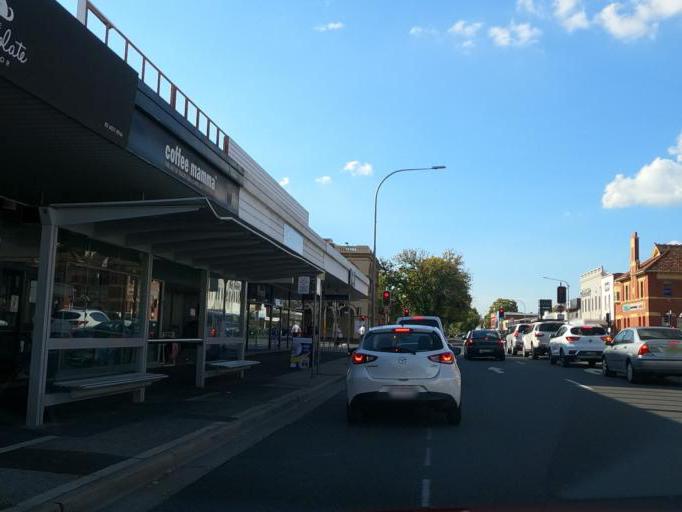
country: AU
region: New South Wales
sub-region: Albury Municipality
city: Albury
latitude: -36.0815
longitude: 146.9180
